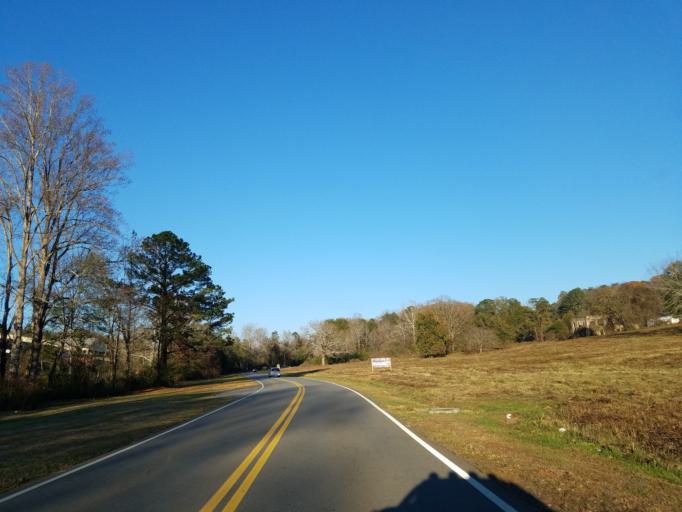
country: US
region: Georgia
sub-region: Cherokee County
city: Ball Ground
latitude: 34.3302
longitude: -84.3848
